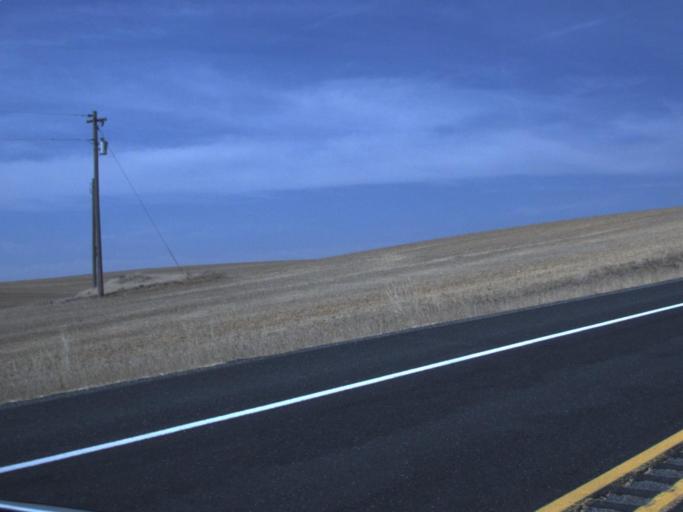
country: US
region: Washington
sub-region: Spokane County
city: Veradale
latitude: 47.4966
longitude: -117.1538
